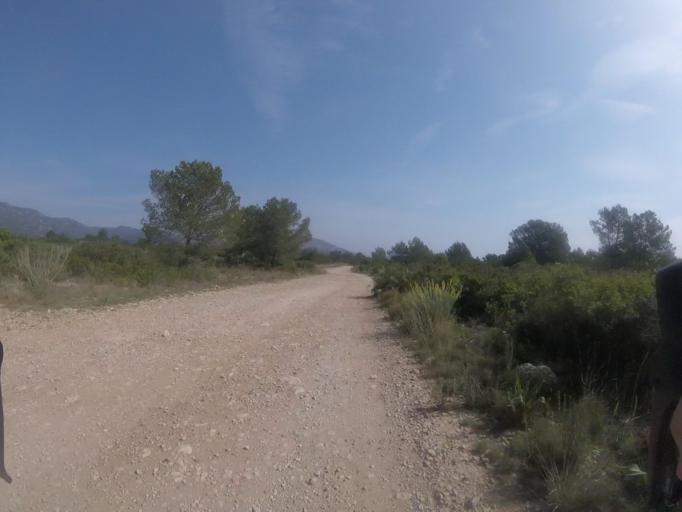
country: ES
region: Valencia
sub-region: Provincia de Castello
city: Alcoceber
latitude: 40.2796
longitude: 0.3208
